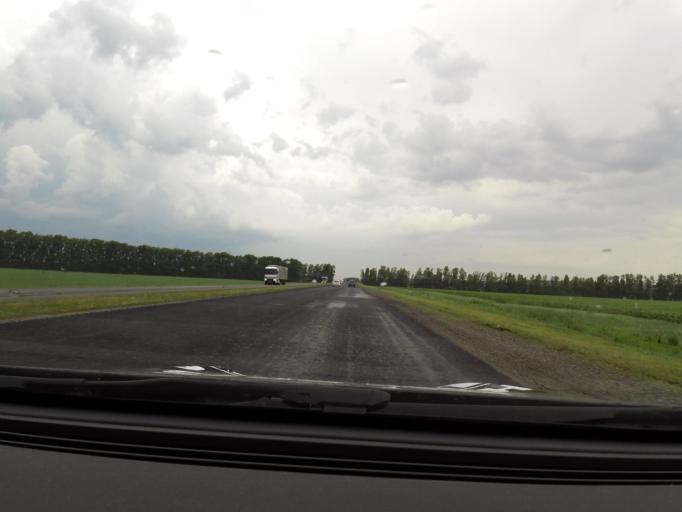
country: RU
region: Bashkortostan
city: Asanovo
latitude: 54.9434
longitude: 55.5815
